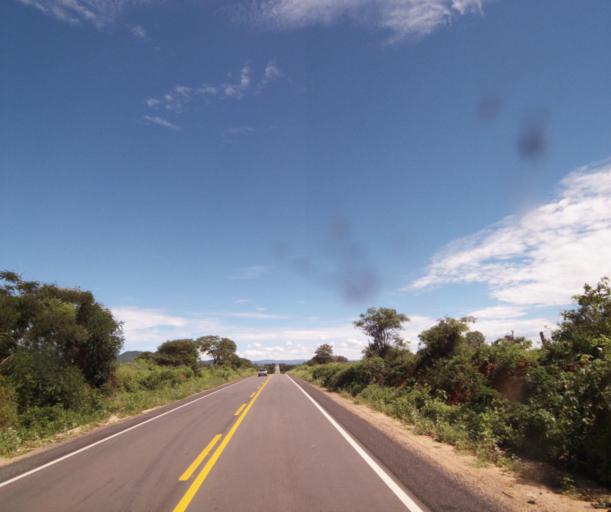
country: BR
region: Bahia
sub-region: Guanambi
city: Guanambi
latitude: -14.4054
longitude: -42.7448
